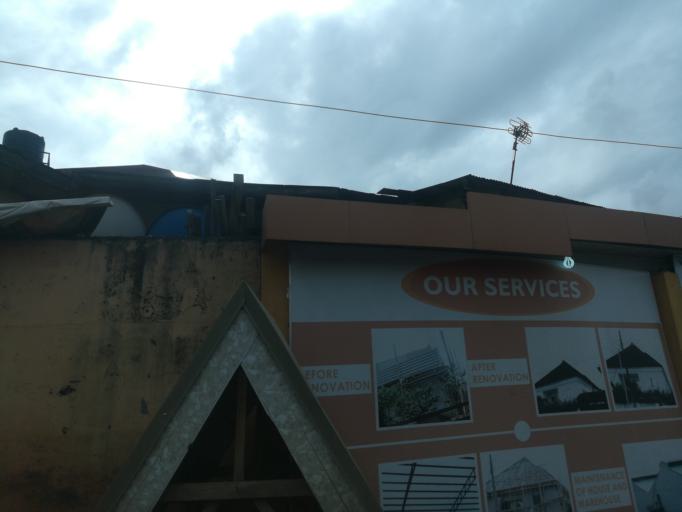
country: NG
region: Lagos
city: Ikeja
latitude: 6.6008
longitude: 3.3366
